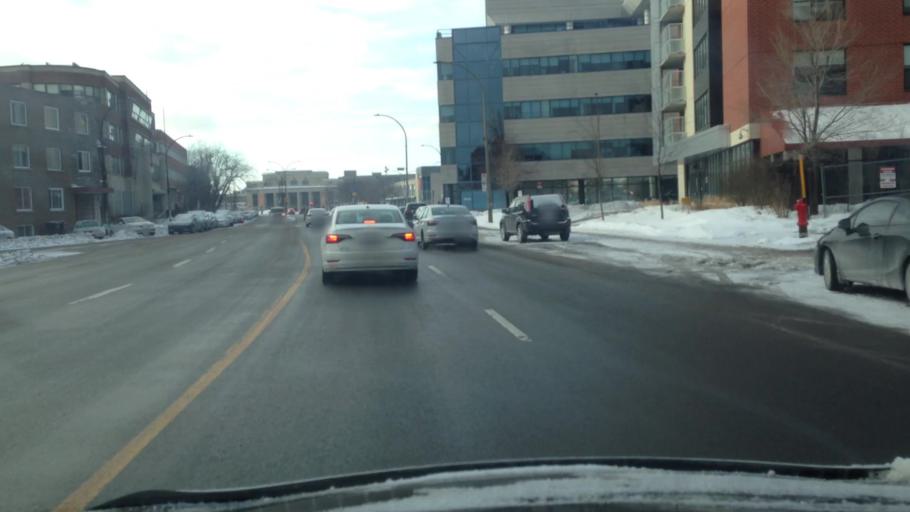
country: CA
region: Quebec
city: Mont-Royal
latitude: 45.5295
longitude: -73.6187
